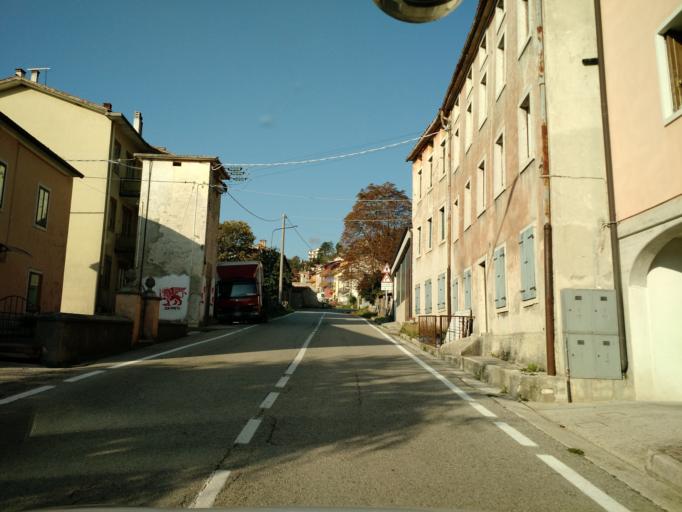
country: IT
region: Veneto
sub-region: Provincia di Vicenza
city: Lusiana
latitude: 45.7898
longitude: 11.5580
